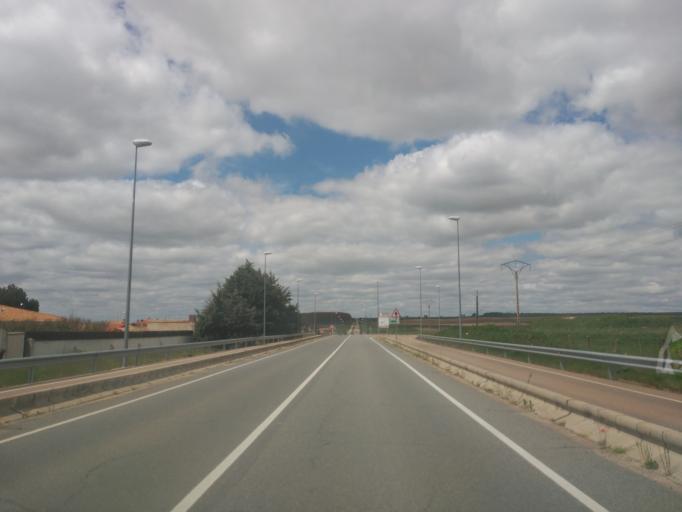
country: ES
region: Castille and Leon
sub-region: Provincia de Salamanca
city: Villamayor
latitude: 41.0158
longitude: -5.7140
